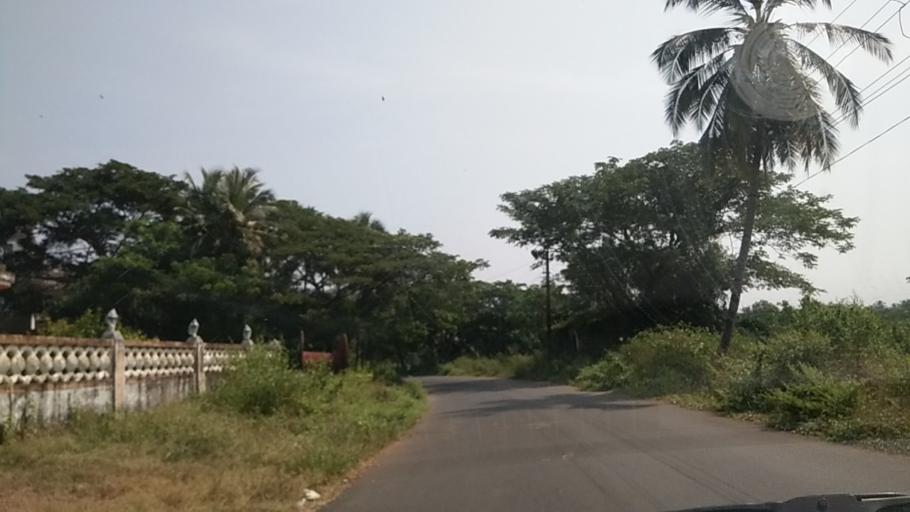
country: IN
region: Goa
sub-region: North Goa
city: Goa Velha
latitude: 15.4419
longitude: 73.8636
